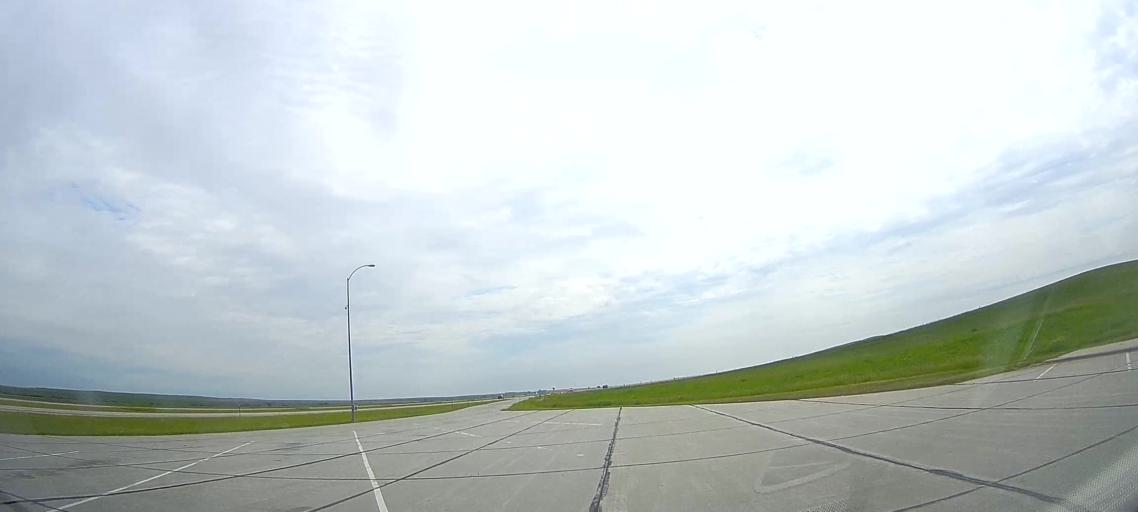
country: US
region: South Dakota
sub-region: Lyman County
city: Kennebec
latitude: 43.9118
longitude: -100.1989
